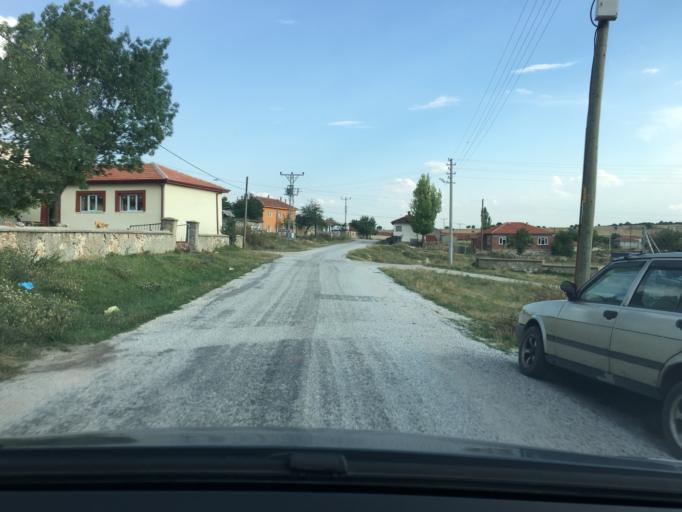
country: TR
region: Eskisehir
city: Kirka
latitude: 39.2763
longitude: 30.6766
